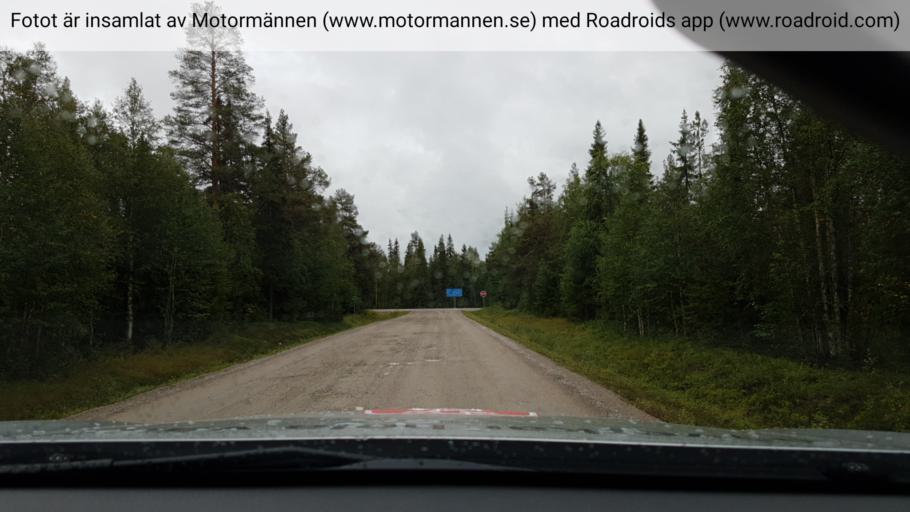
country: SE
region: Vaesterbotten
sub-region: Asele Kommun
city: Insjon
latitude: 64.7213
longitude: 17.6583
